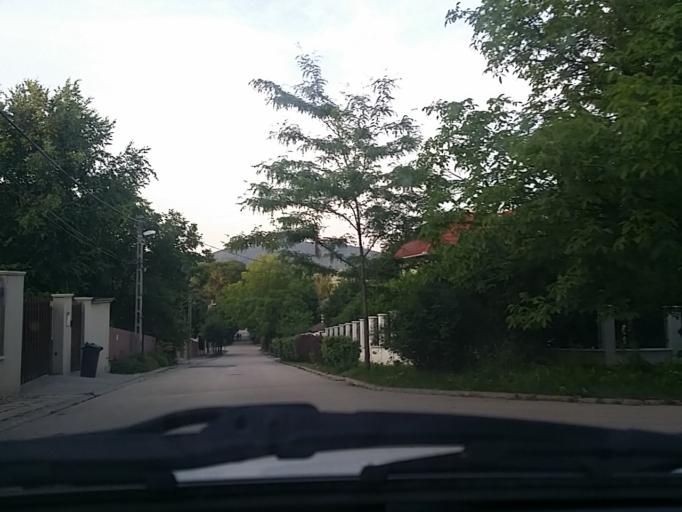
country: HU
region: Pest
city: Solymar
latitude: 47.5597
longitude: 18.9550
